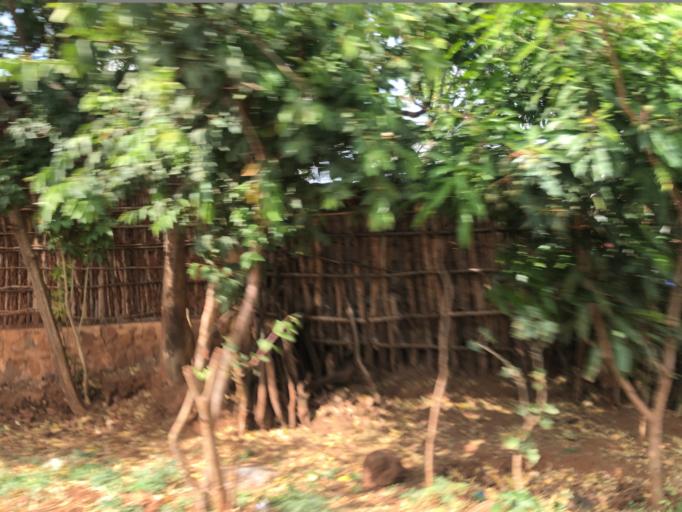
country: ET
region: Southern Nations, Nationalities, and People's Region
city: Konso
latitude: 5.3300
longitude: 37.4071
